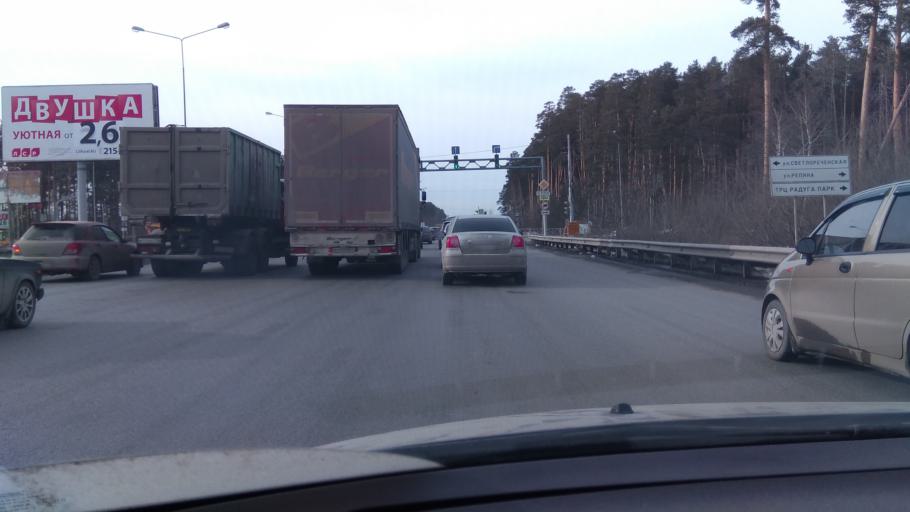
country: RU
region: Sverdlovsk
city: Shirokaya Rechka
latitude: 56.8125
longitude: 60.5188
